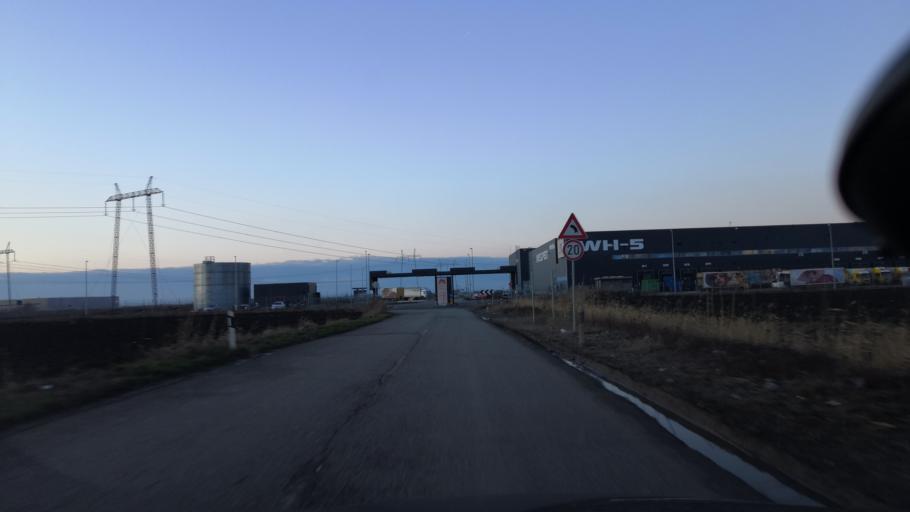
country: RS
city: Simanovci
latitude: 44.8906
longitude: 20.1091
